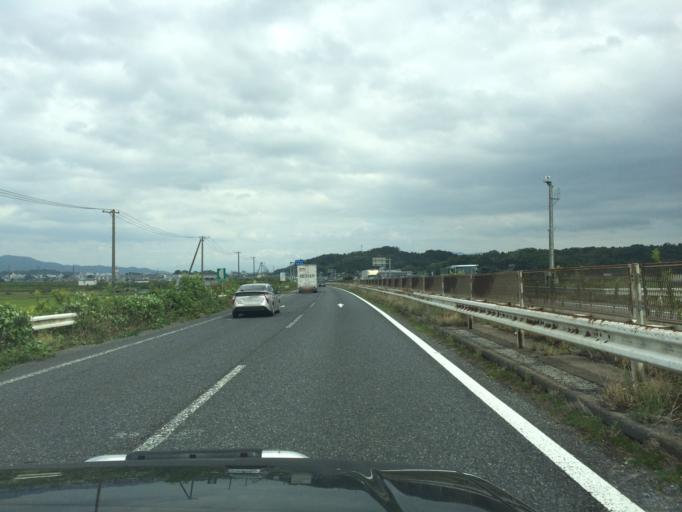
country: JP
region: Mie
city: Ueno-ebisumachi
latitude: 34.7408
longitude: 136.1141
